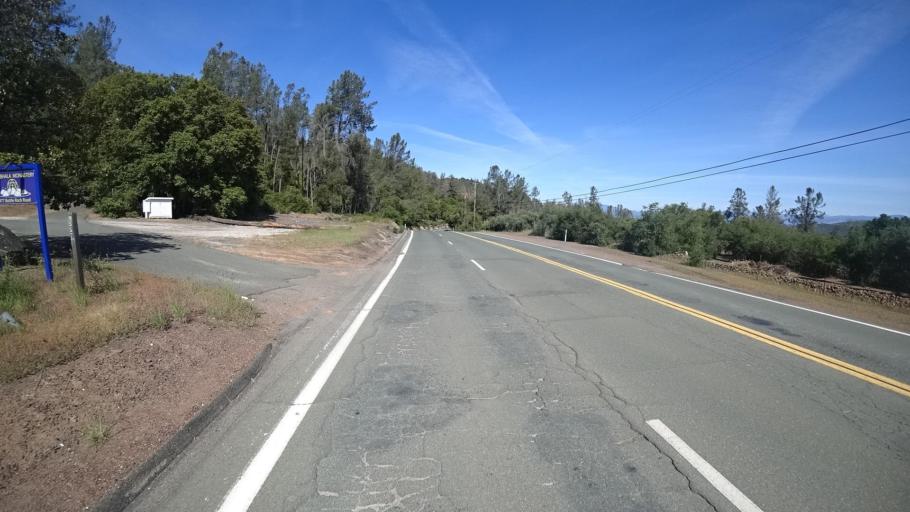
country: US
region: California
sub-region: Lake County
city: Kelseyville
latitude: 38.9161
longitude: -122.8015
